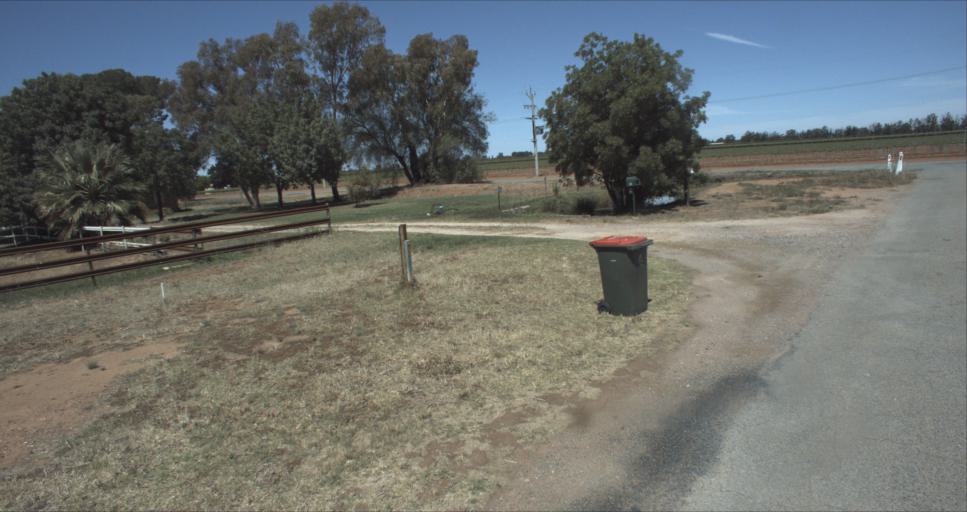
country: AU
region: New South Wales
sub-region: Leeton
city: Leeton
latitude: -34.5306
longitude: 146.3332
